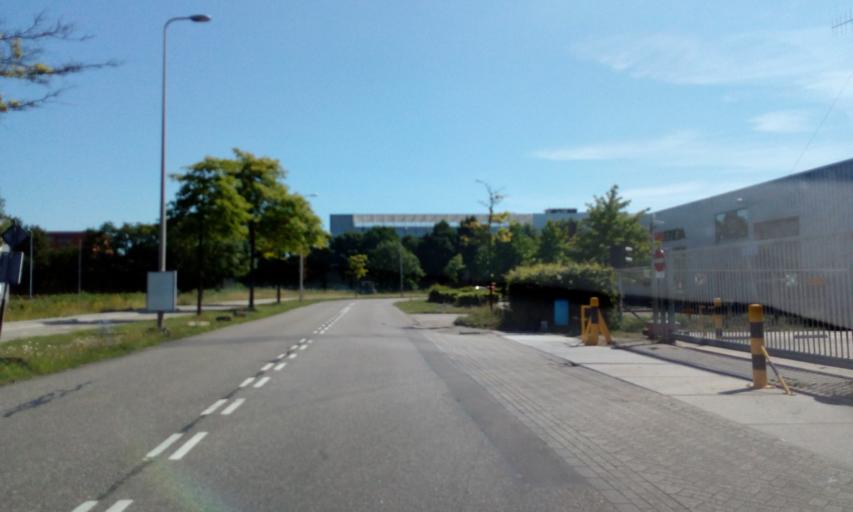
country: NL
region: South Holland
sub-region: Gemeente Alphen aan den Rijn
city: Alphen aan den Rijn
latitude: 52.1326
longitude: 4.6300
